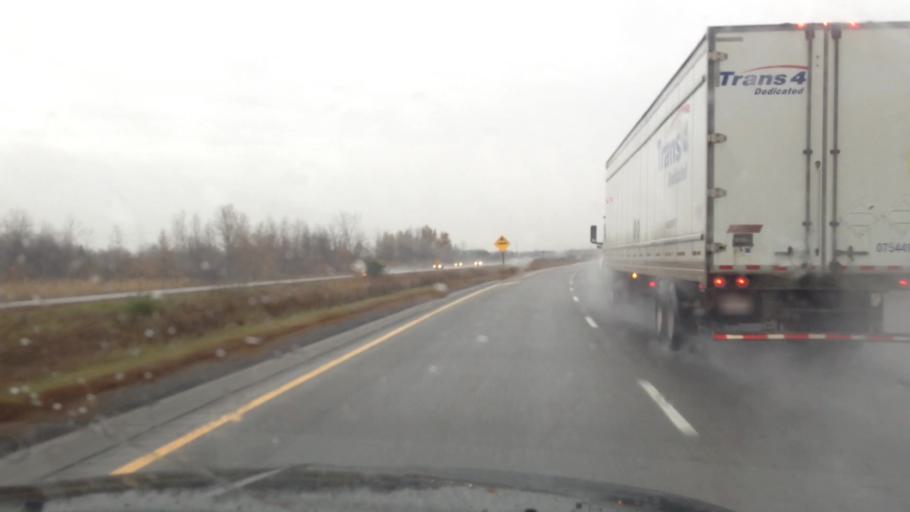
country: CA
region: Ontario
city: Casselman
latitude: 45.3138
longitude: -75.1566
